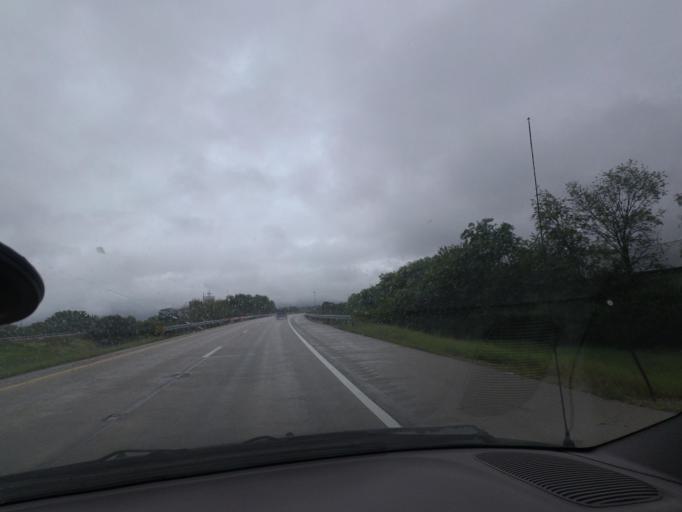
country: US
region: Illinois
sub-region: Champaign County
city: Champaign
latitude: 40.1191
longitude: -88.2896
